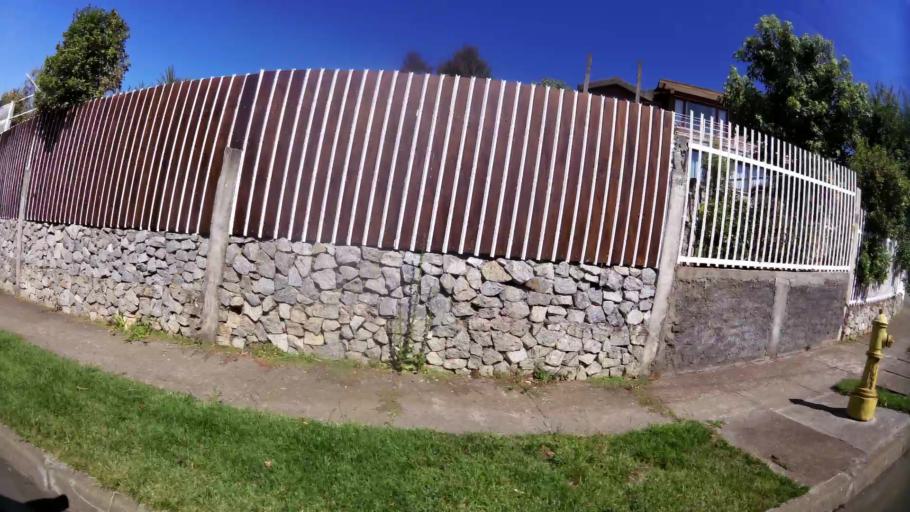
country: CL
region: Biobio
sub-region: Provincia de Concepcion
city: Concepcion
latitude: -36.7837
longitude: -73.0502
